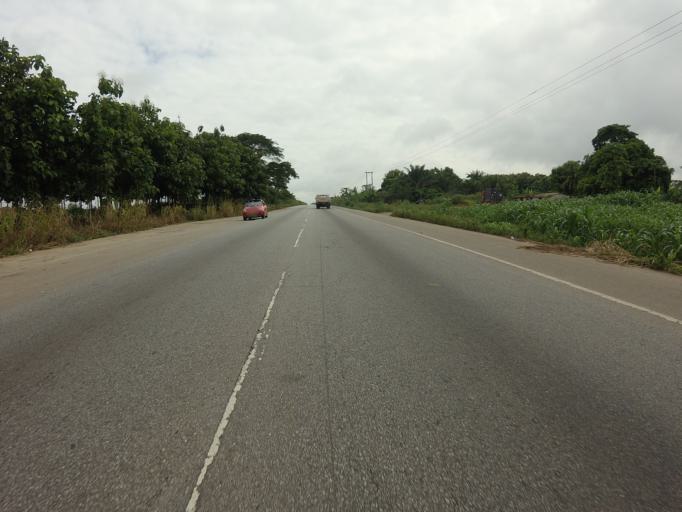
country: GH
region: Ashanti
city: Tafo
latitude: 6.9776
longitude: -1.6865
